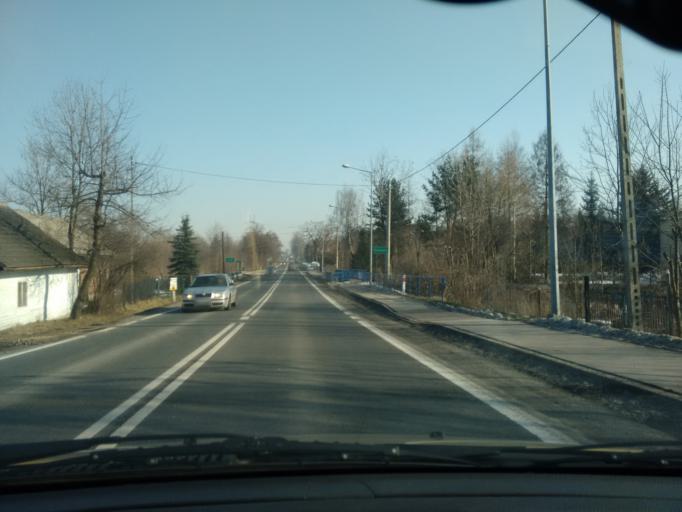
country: PL
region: Lesser Poland Voivodeship
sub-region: Powiat oswiecimski
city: Kety
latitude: 49.8809
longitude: 19.2511
